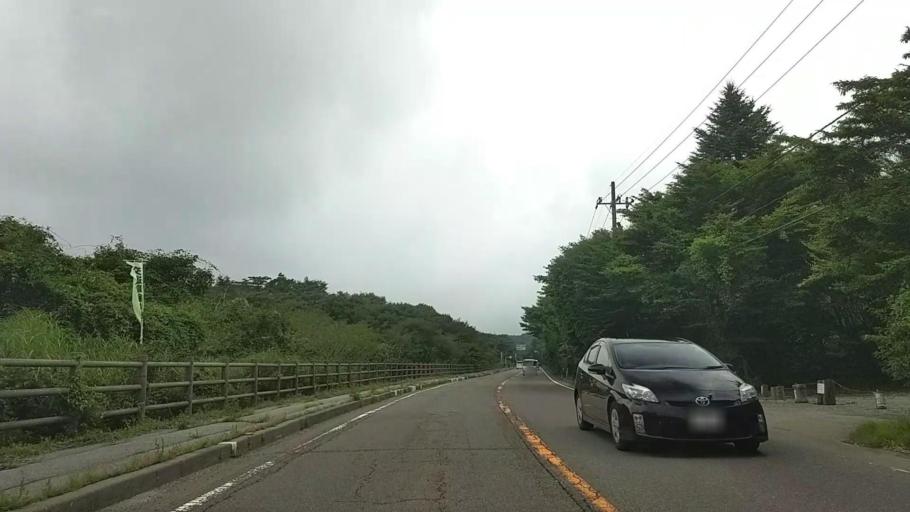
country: JP
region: Yamanashi
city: Fujikawaguchiko
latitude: 35.4376
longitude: 138.6015
